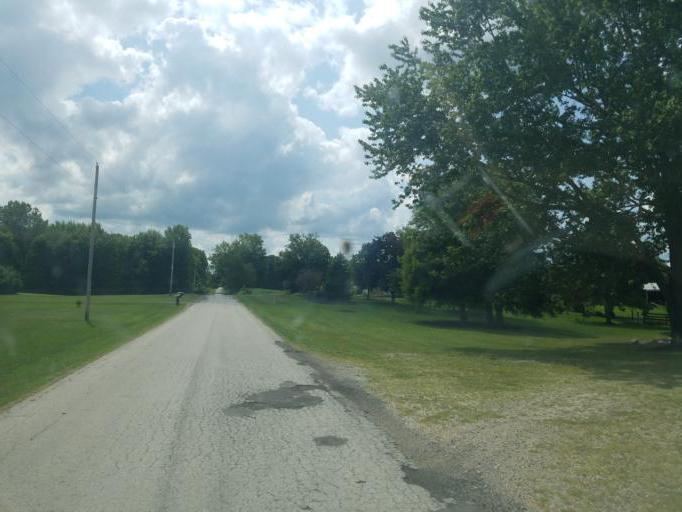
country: US
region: Ohio
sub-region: Morrow County
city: Mount Gilead
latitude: 40.4403
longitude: -82.7467
